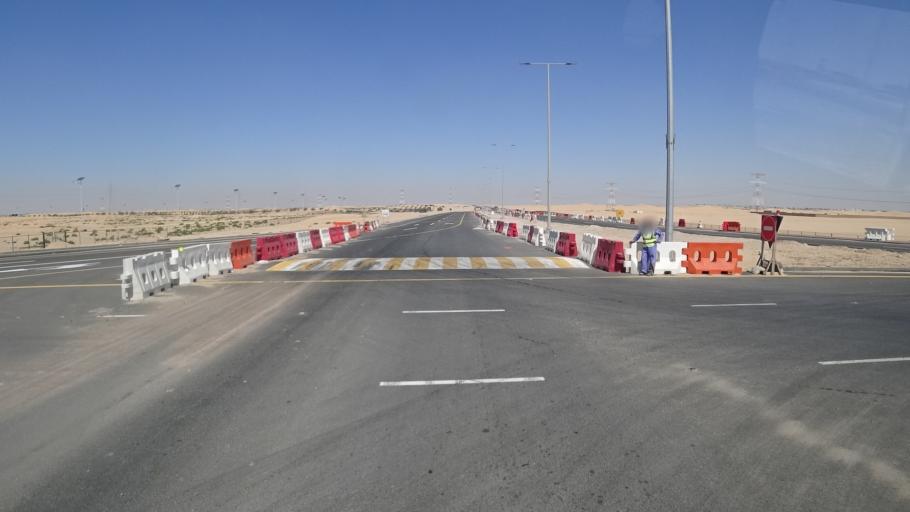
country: AE
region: Abu Dhabi
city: Abu Dhabi
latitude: 24.1734
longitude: 54.8502
